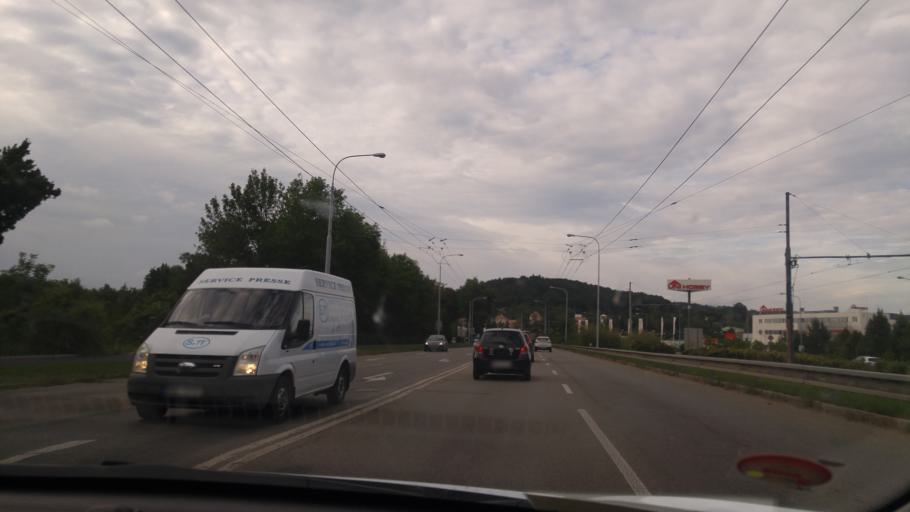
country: CZ
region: South Moravian
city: Troubsko
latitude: 49.2230
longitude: 16.5363
